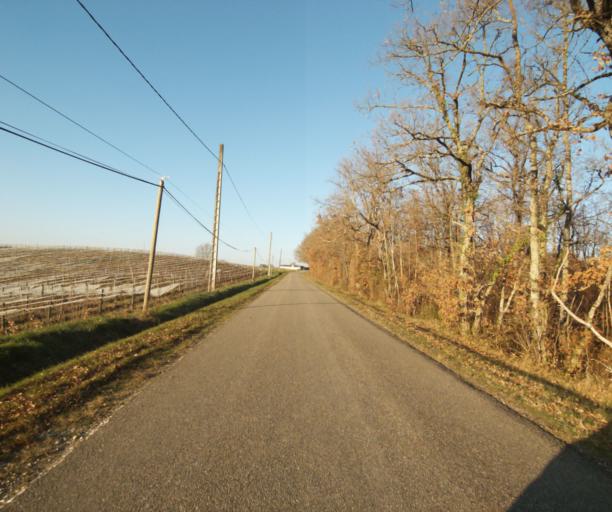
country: FR
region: Midi-Pyrenees
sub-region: Departement du Tarn-et-Garonne
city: Moissac
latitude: 44.1403
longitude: 1.1216
